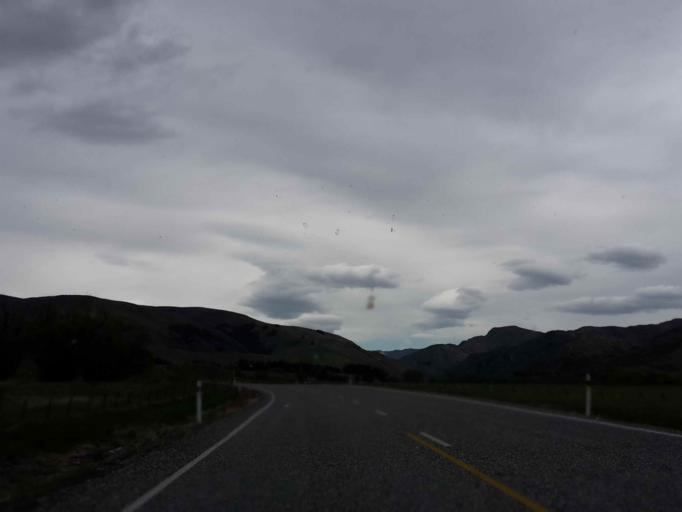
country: NZ
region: Otago
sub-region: Queenstown-Lakes District
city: Wanaka
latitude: -44.6607
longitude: 169.4892
